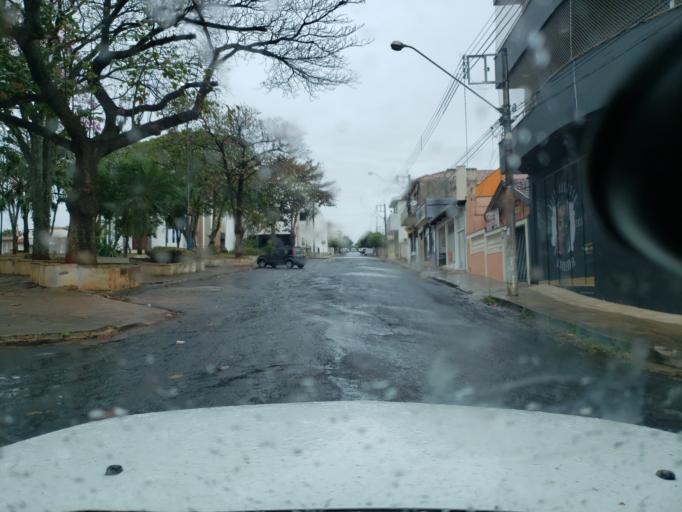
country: BR
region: Sao Paulo
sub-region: Moji-Guacu
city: Mogi-Gaucu
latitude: -22.3762
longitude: -46.9367
